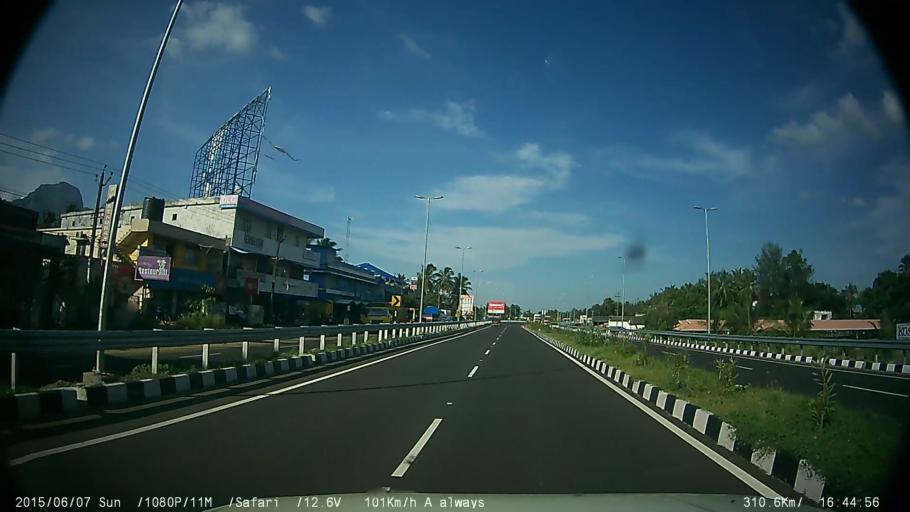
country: IN
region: Kerala
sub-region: Palakkad district
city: Palakkad
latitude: 10.7964
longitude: 76.7388
